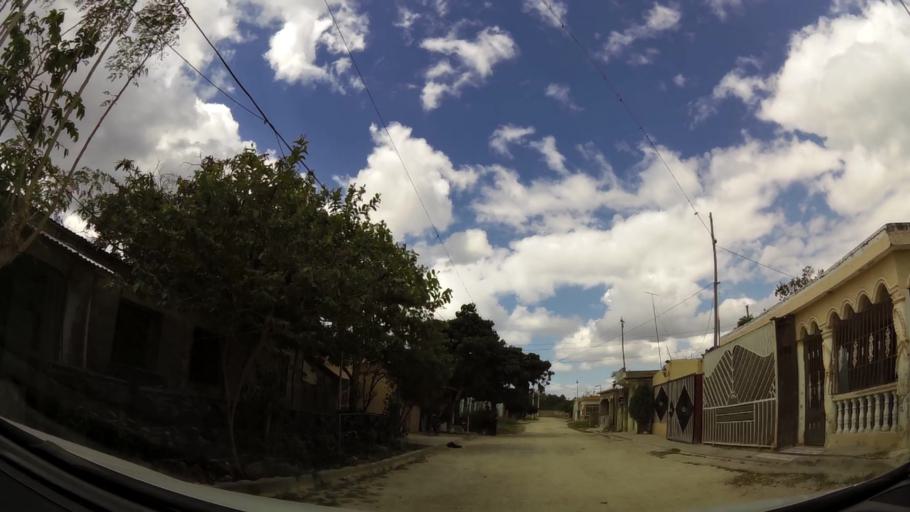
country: DO
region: Santo Domingo
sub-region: Santo Domingo
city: Boca Chica
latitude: 18.4510
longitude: -69.6472
